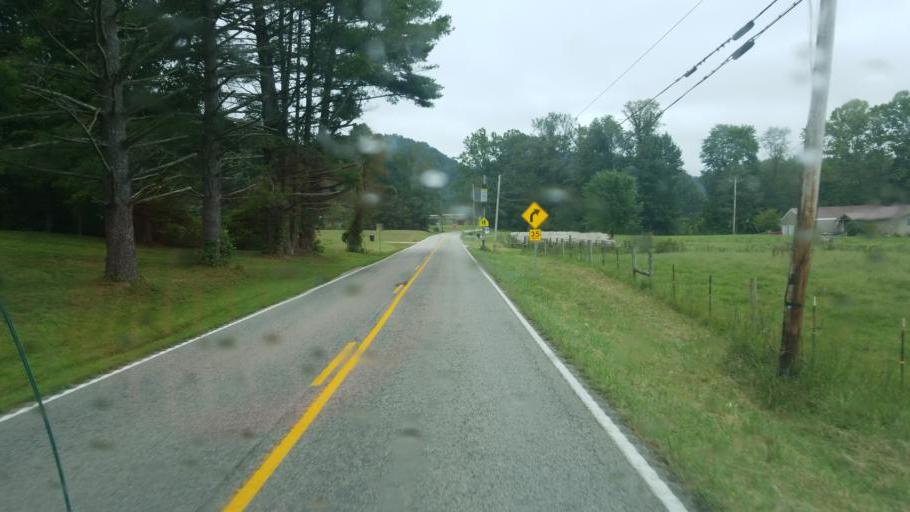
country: US
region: Kentucky
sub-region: Rowan County
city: Morehead
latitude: 38.2703
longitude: -83.4280
